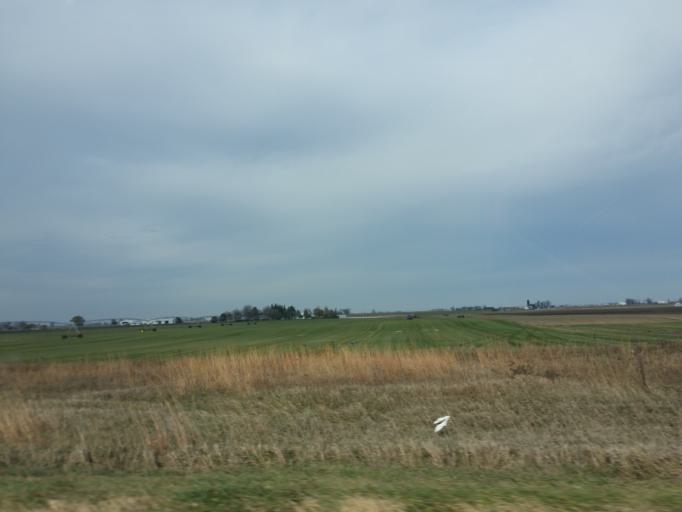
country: US
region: Iowa
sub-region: Scott County
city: Eldridge
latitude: 41.6023
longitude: -90.6515
